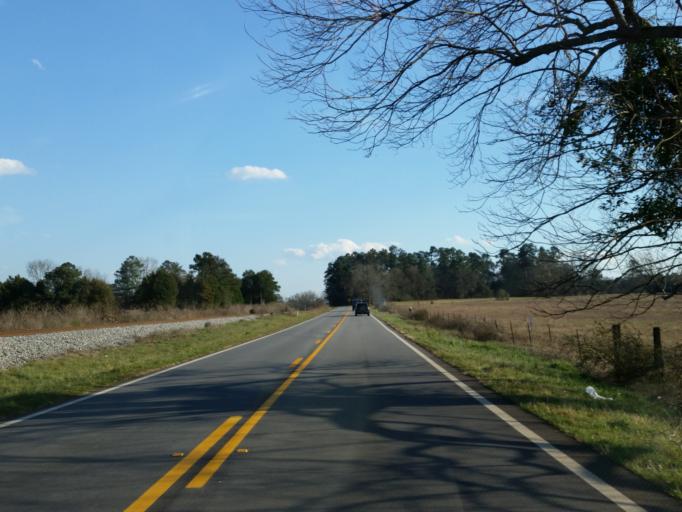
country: US
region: Georgia
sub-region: Monroe County
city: Forsyth
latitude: 33.0020
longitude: -83.9027
